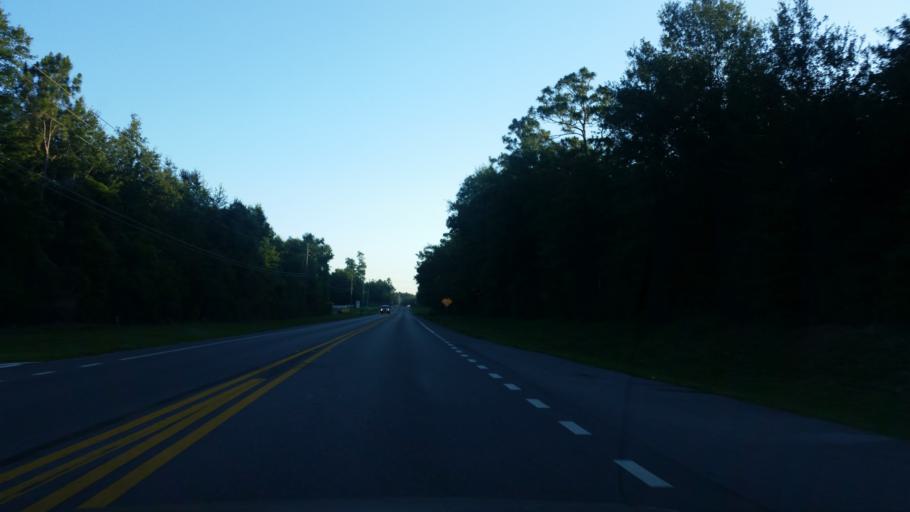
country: US
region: Florida
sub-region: Escambia County
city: Cantonment
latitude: 30.5896
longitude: -87.3282
